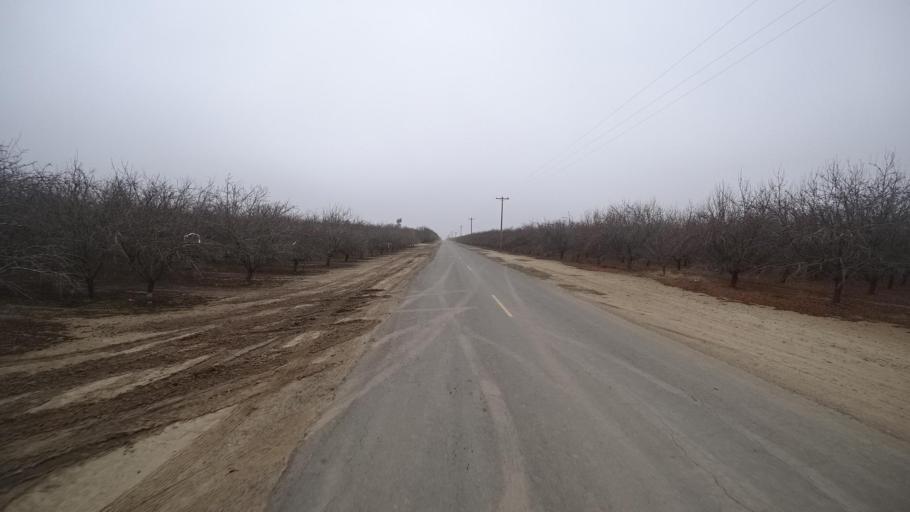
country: US
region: California
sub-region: Kern County
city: Wasco
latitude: 35.5931
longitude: -119.5092
